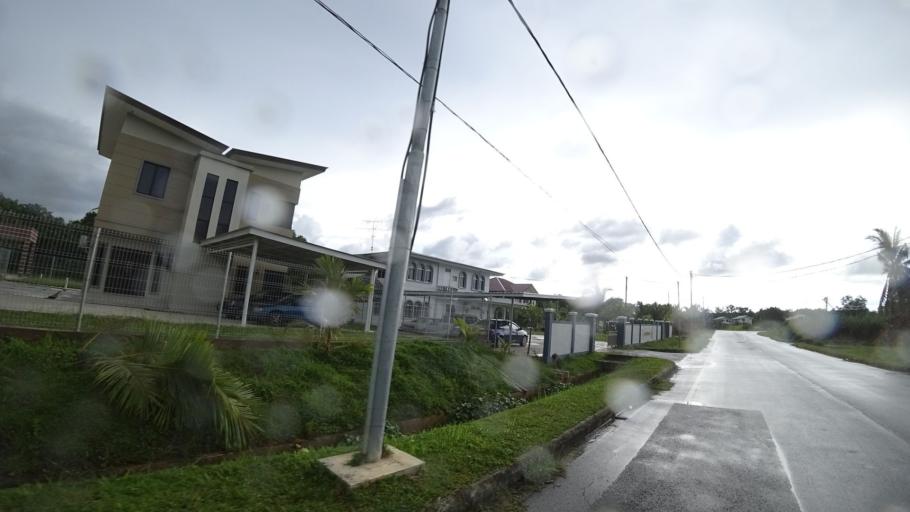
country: BN
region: Brunei and Muara
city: Bandar Seri Begawan
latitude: 4.8355
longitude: 114.9139
